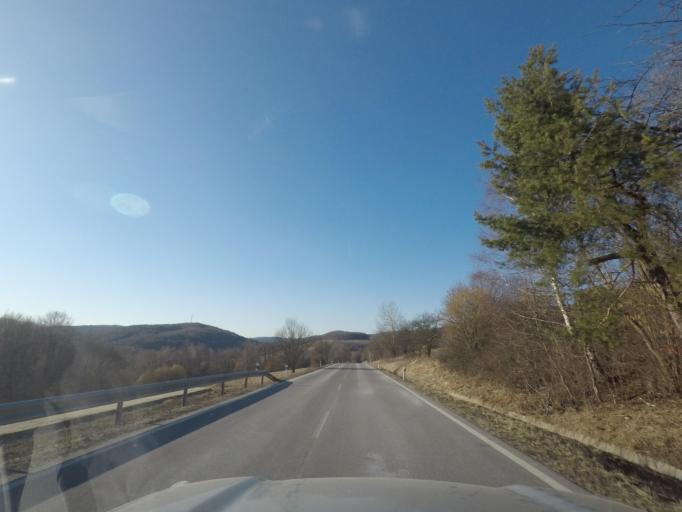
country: SK
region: Presovsky
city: Medzilaborce
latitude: 49.2799
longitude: 21.8560
